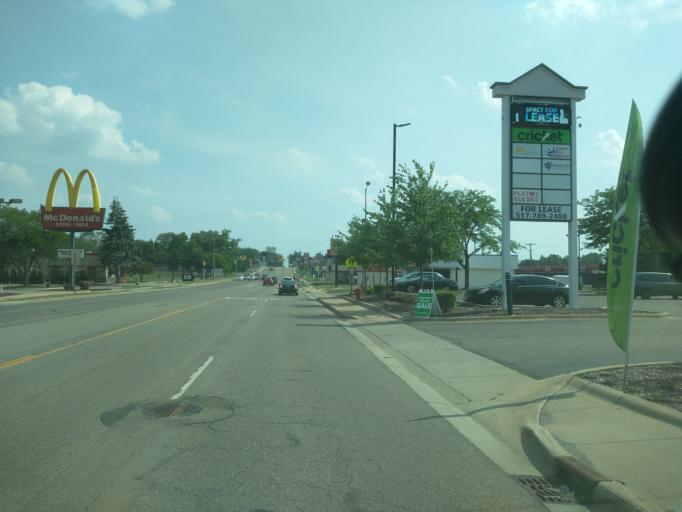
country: US
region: Michigan
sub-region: Jackson County
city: Jackson
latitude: 42.2632
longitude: -84.4235
